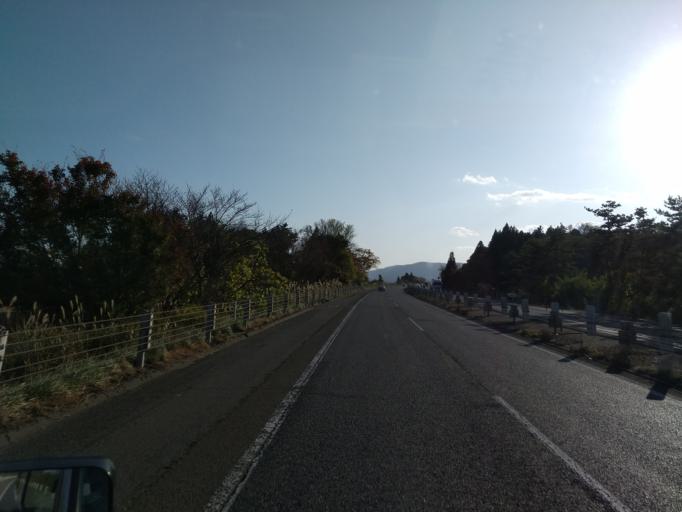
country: JP
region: Iwate
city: Morioka-shi
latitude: 39.6118
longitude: 141.1288
